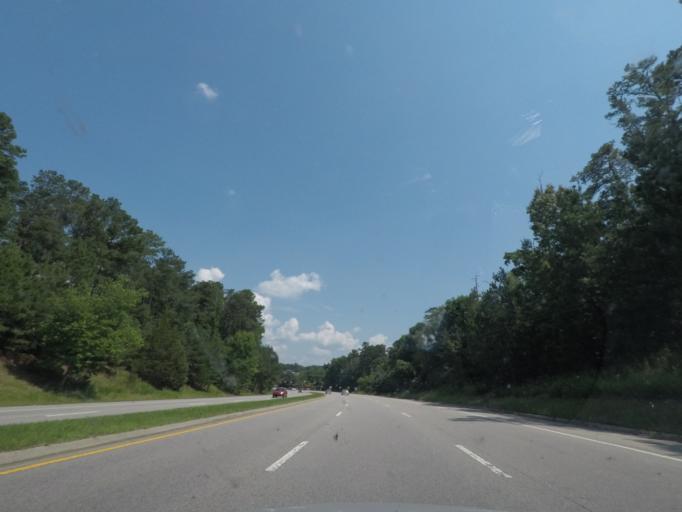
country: US
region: North Carolina
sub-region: Durham County
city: Durham
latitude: 35.9635
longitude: -78.9637
